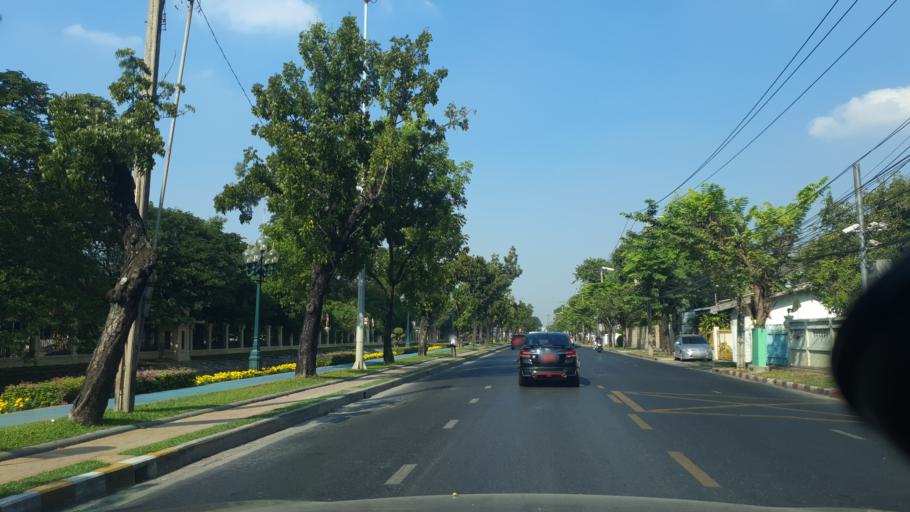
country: TH
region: Bangkok
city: Dusit
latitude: 13.7712
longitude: 100.5243
